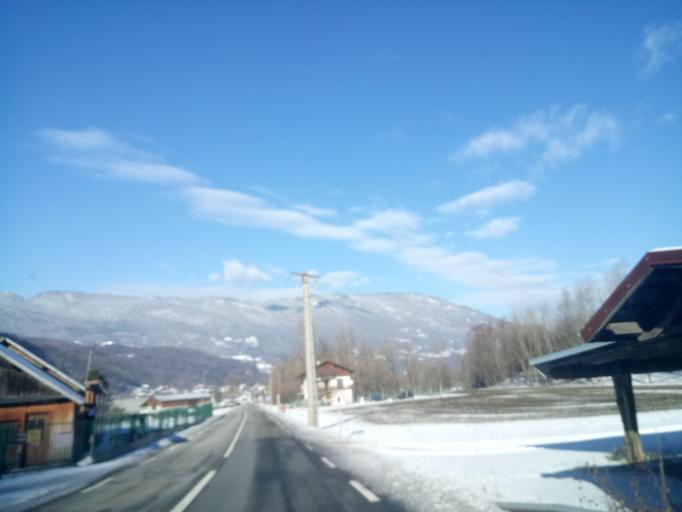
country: FR
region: Rhone-Alpes
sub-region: Departement de la Savoie
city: Saint-Remy-de-Maurienne
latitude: 45.4617
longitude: 6.2904
